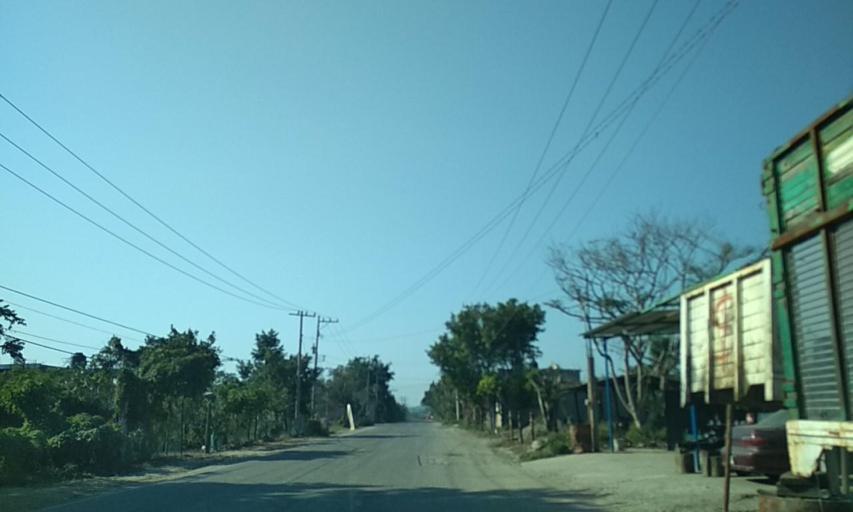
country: MX
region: Veracruz
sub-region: Papantla
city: El Chote
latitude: 20.4056
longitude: -97.3435
